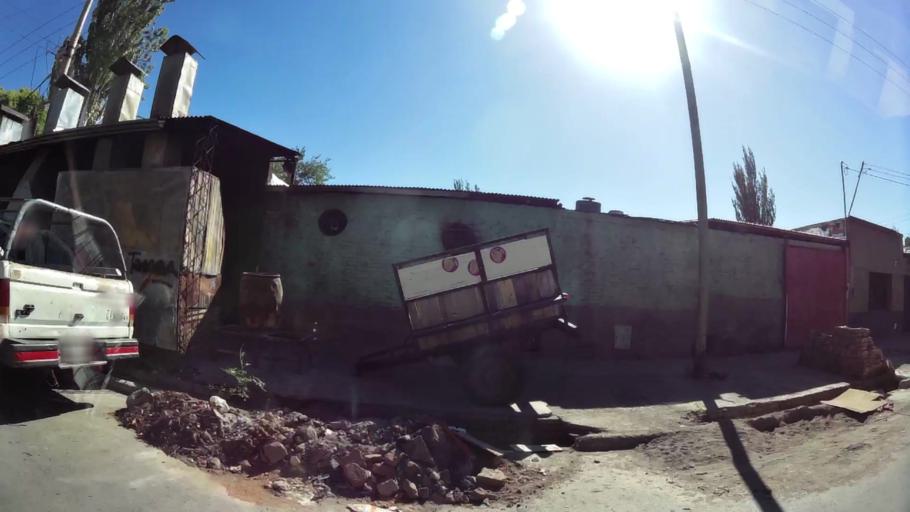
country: AR
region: Mendoza
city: Las Heras
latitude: -32.8418
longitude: -68.8234
